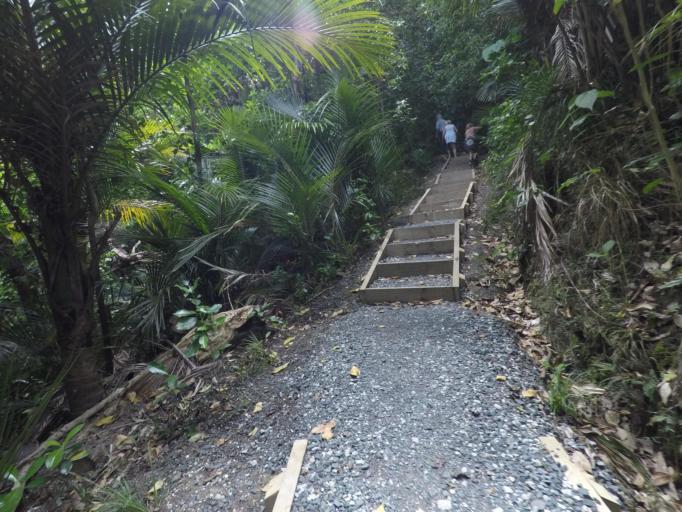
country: NZ
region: Auckland
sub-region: Auckland
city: Warkworth
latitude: -36.5357
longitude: 174.7090
